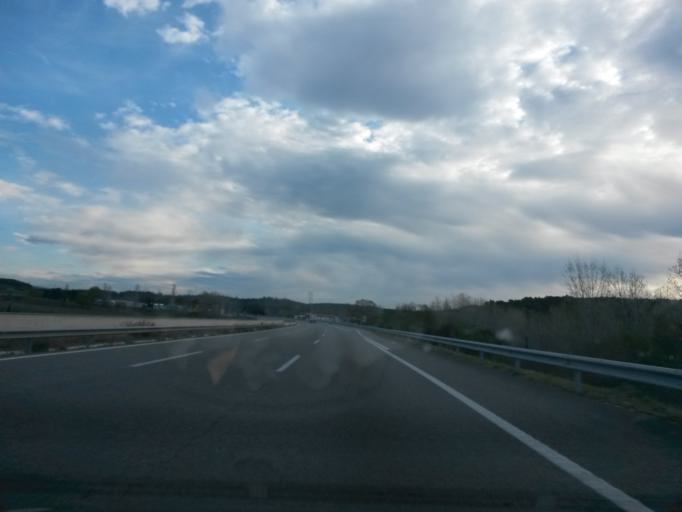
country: ES
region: Catalonia
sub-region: Provincia de Girona
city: Pontos
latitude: 42.1701
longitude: 2.9281
